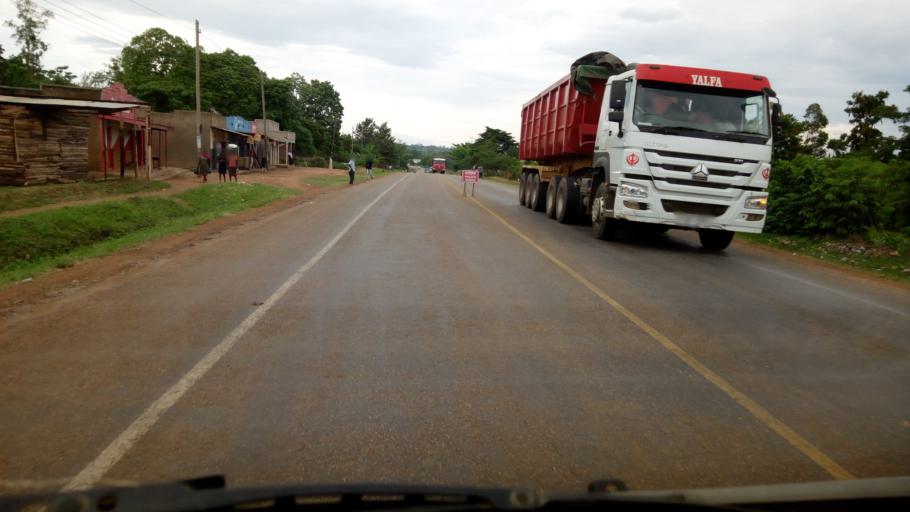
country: UG
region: Eastern Region
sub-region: Mbale District
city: Mbale
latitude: 1.0080
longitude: 34.1709
